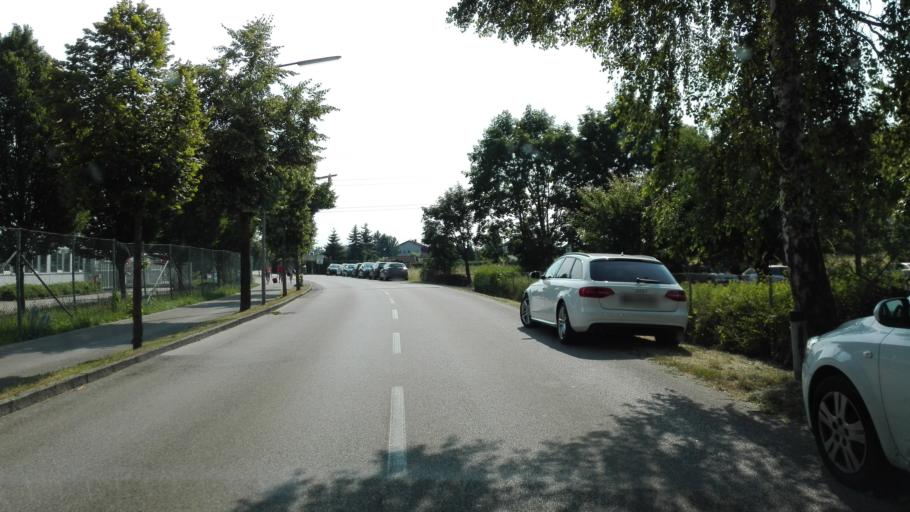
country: AT
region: Upper Austria
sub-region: Politischer Bezirk Linz-Land
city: Traun
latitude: 48.2128
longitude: 14.2173
